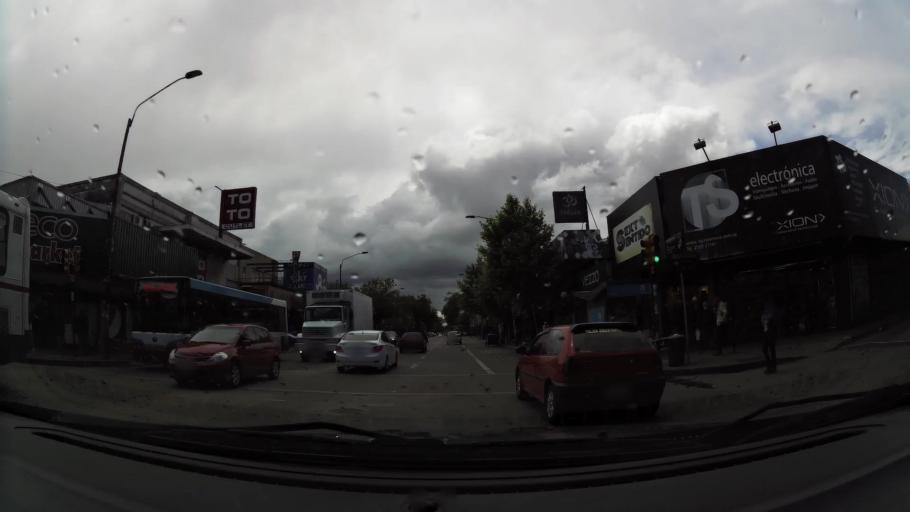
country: UY
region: Montevideo
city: Montevideo
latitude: -34.8764
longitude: -56.1429
